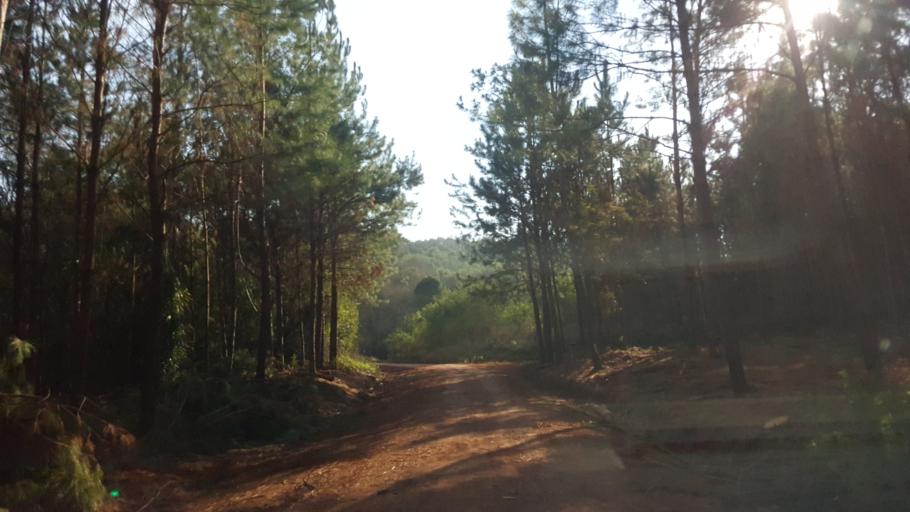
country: AR
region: Misiones
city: Capiovi
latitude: -26.9014
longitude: -55.0919
